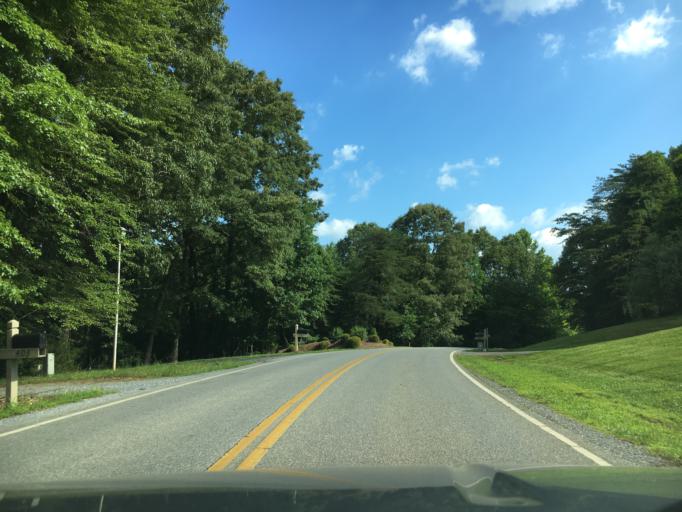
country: US
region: Virginia
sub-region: Bedford County
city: Forest
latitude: 37.3899
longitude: -79.2558
